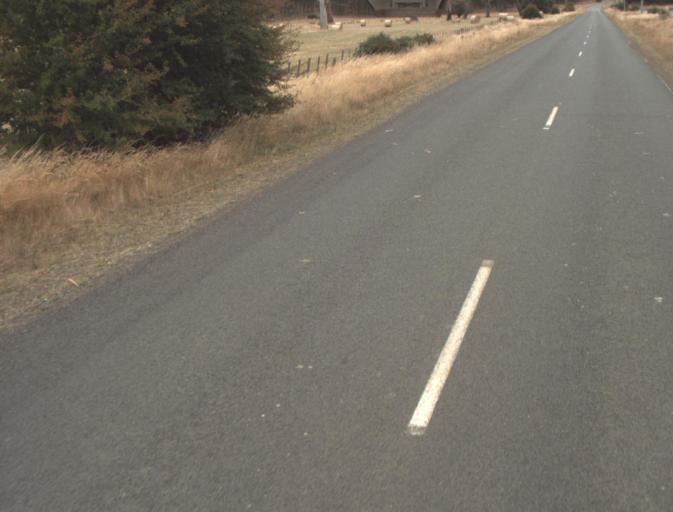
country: AU
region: Tasmania
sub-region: Northern Midlands
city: Evandale
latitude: -41.5033
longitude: 147.4853
